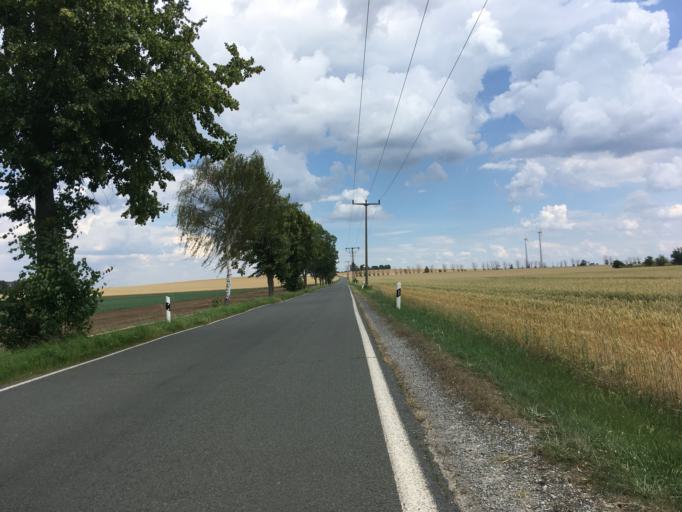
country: DE
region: Saxony-Anhalt
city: Baalberge
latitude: 51.7748
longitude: 11.8305
